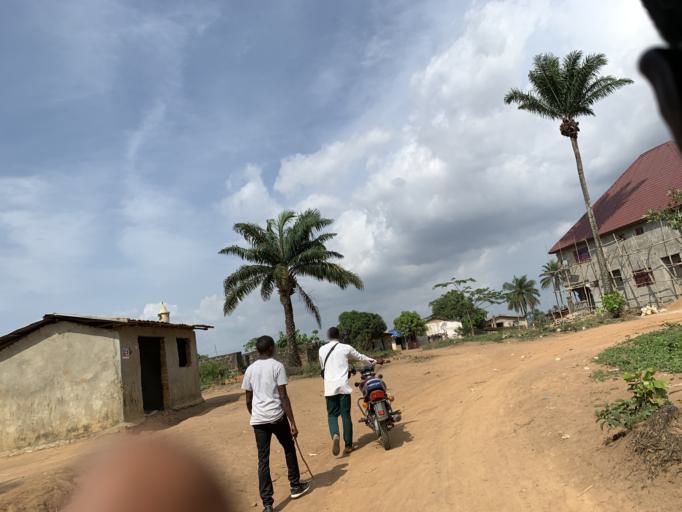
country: SL
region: Western Area
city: Waterloo
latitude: 8.3508
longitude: -13.0430
